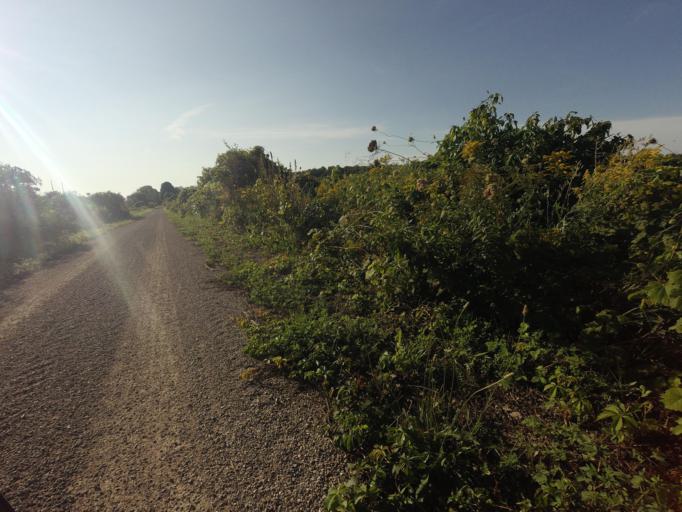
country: CA
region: Ontario
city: Goderich
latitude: 43.7529
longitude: -81.5077
